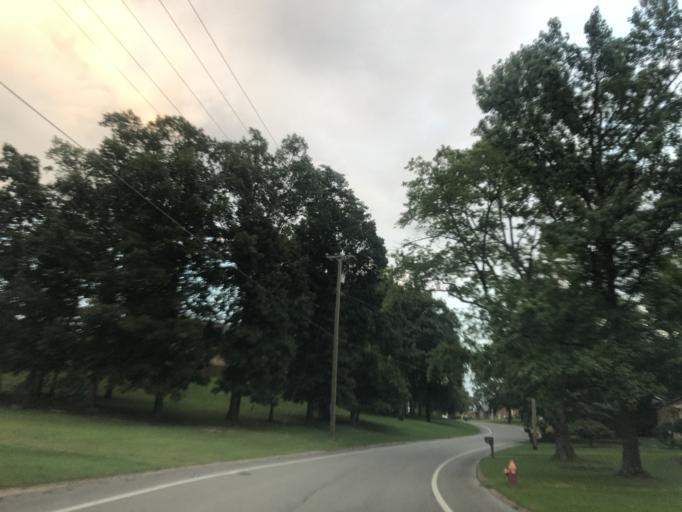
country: US
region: Tennessee
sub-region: Davidson County
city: Lakewood
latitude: 36.1485
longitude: -86.6351
